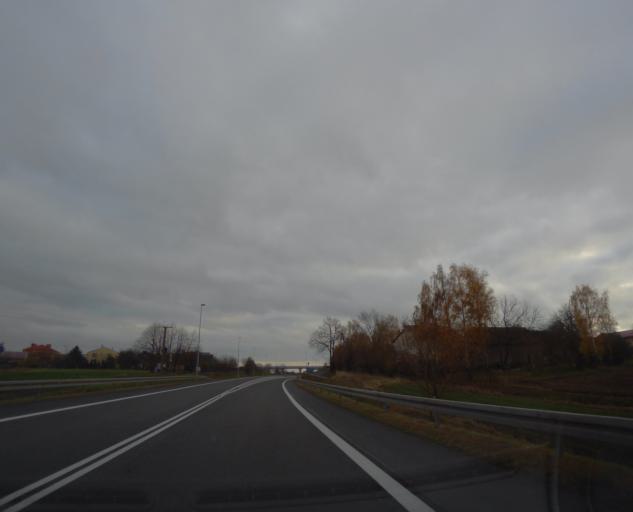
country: PL
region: Subcarpathian Voivodeship
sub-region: Powiat jaroslawski
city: Radymno
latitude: 49.9357
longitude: 22.8164
